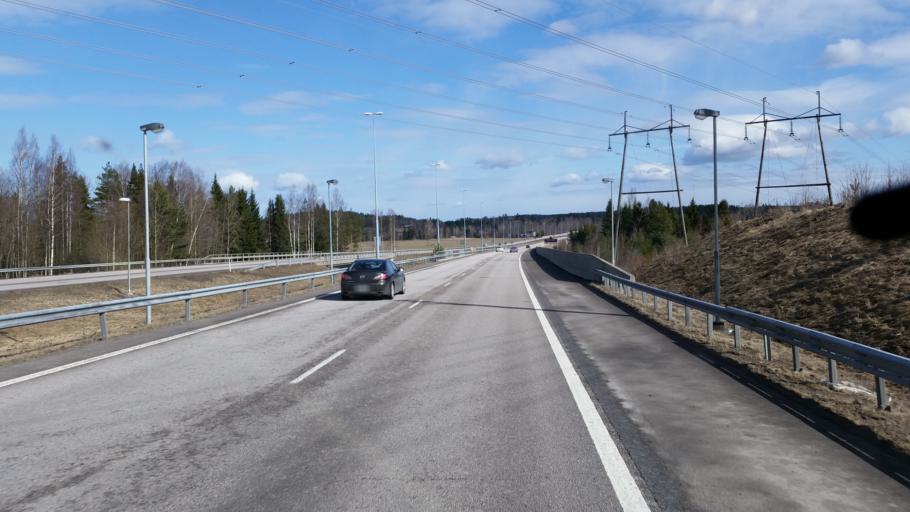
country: FI
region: Uusimaa
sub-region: Porvoo
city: Porvoo
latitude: 60.4017
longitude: 25.6283
